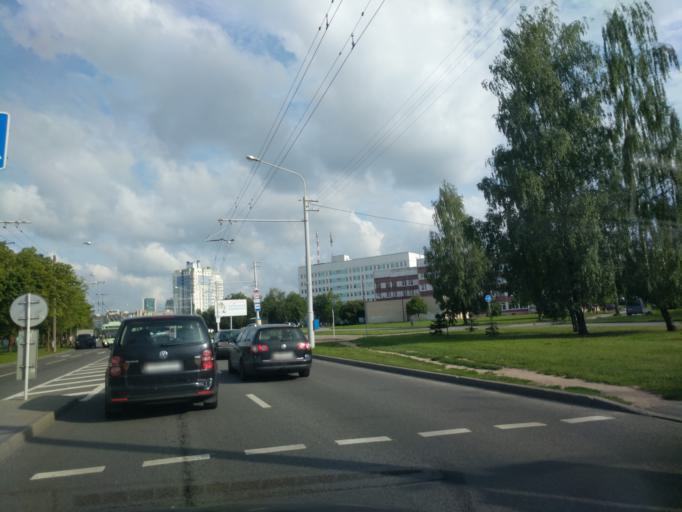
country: BY
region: Minsk
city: Novoye Medvezhino
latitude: 53.8677
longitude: 27.4642
